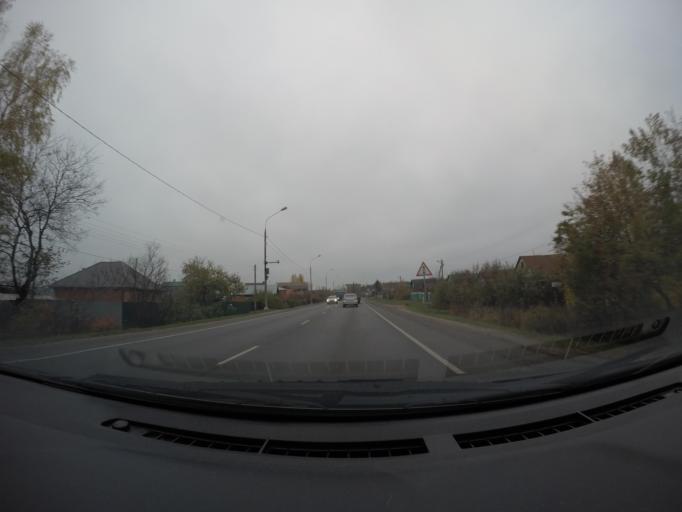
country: RU
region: Moskovskaya
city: Malyshevo
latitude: 55.4689
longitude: 38.3387
